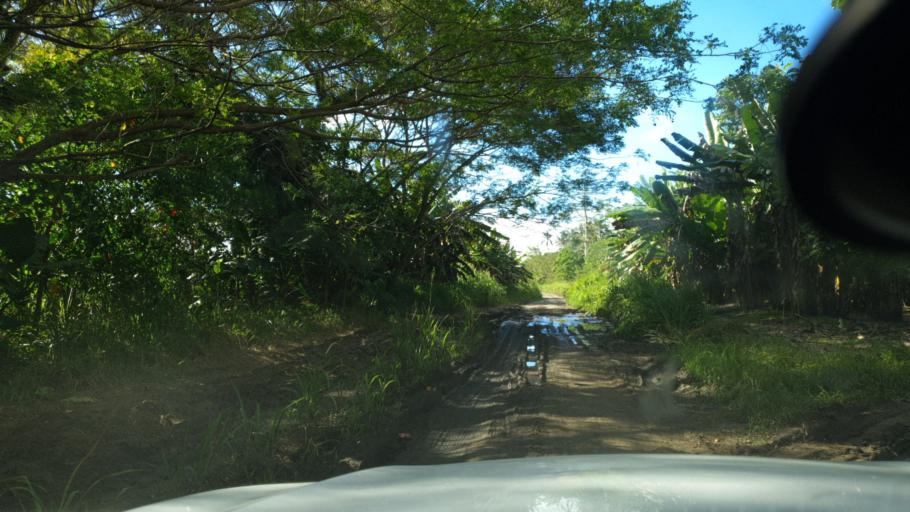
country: SB
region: Guadalcanal
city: Honiara
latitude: -9.4432
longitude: 160.1842
